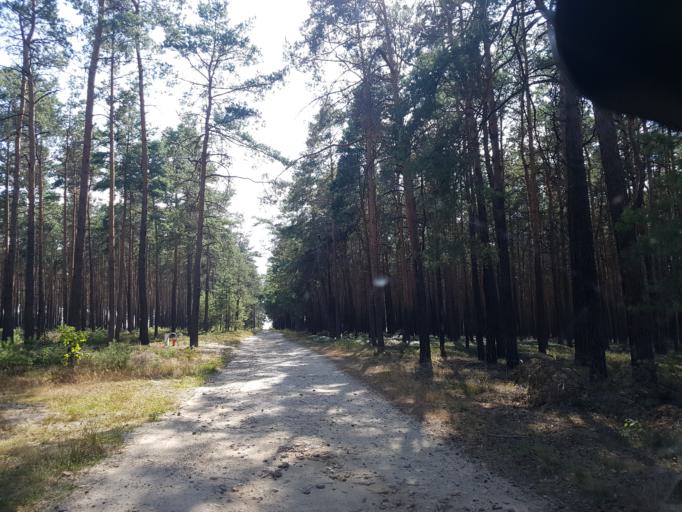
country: DE
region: Brandenburg
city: Finsterwalde
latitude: 51.6402
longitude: 13.7777
